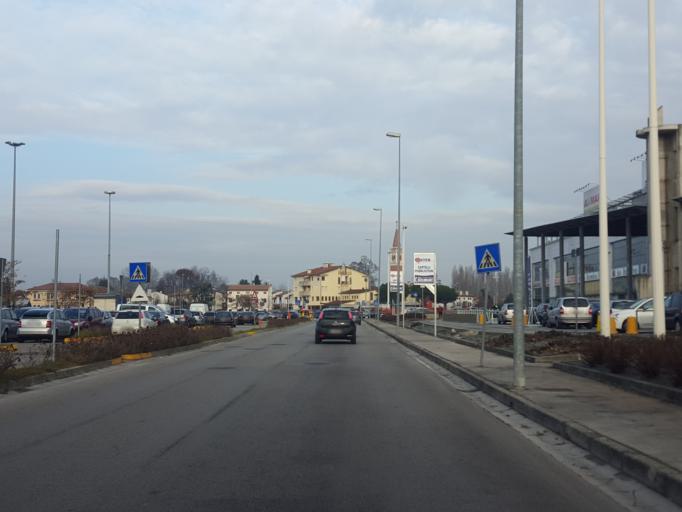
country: IT
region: Veneto
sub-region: Provincia di Vicenza
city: Villaggio Montegrappa
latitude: 45.5258
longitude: 11.5984
